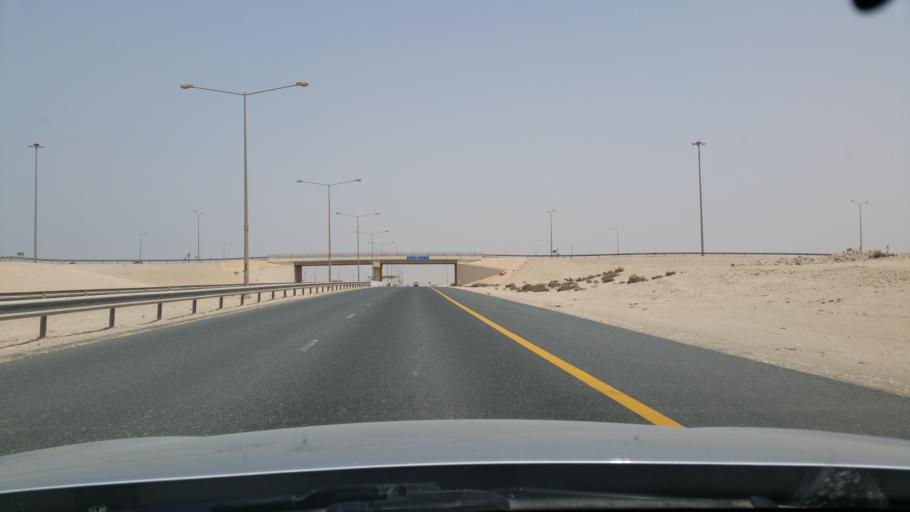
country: QA
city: Umm Bab
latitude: 25.2920
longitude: 50.7912
